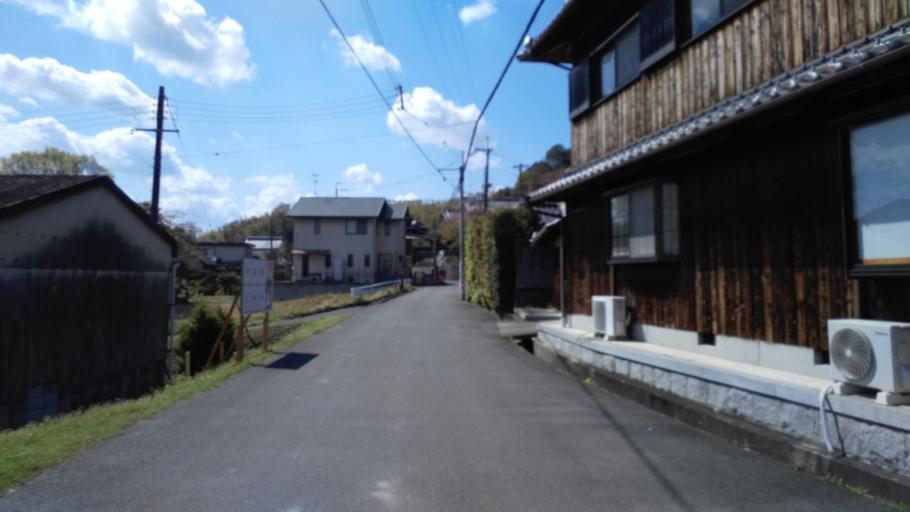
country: JP
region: Kyoto
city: Tanabe
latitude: 34.7866
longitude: 135.7819
